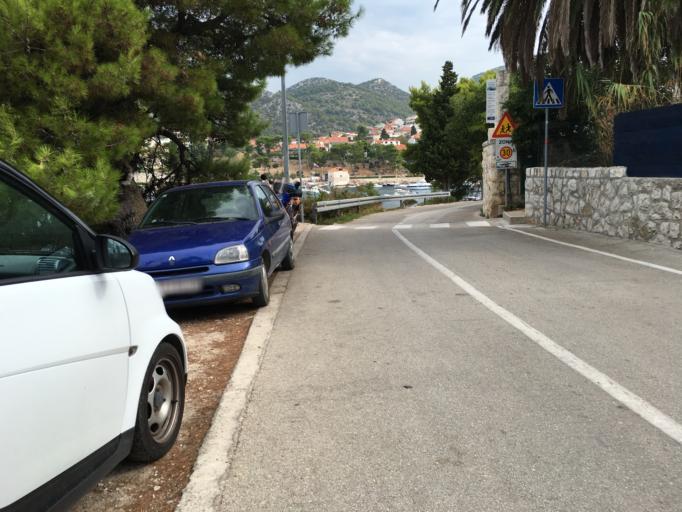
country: HR
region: Splitsko-Dalmatinska
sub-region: Grad Hvar
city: Hvar
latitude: 43.1656
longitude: 16.4419
